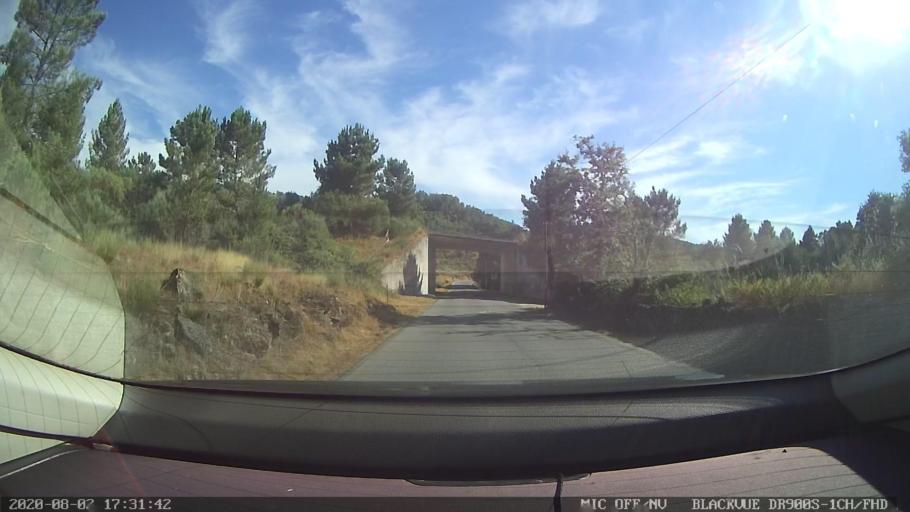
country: PT
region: Vila Real
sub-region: Sabrosa
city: Sabrosa
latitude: 41.3580
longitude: -7.5733
